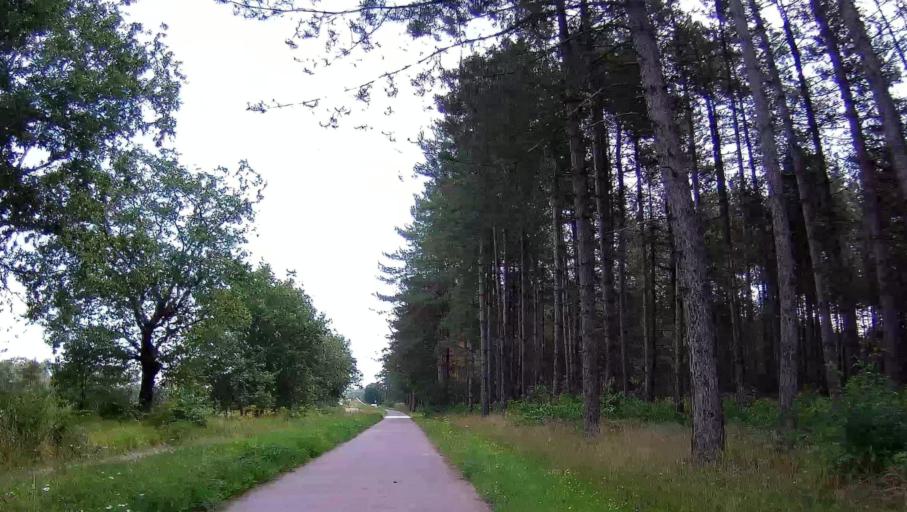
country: BE
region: Flanders
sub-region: Provincie Limburg
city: Lommel
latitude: 51.1975
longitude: 5.2843
